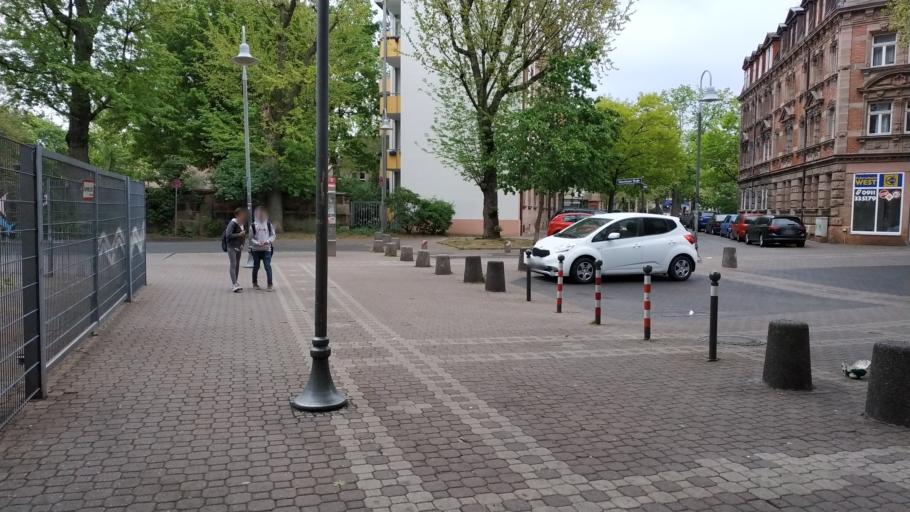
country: DE
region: Bavaria
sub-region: Regierungsbezirk Mittelfranken
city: Grossreuth bei Schweinau
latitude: 49.4403
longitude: 11.0502
